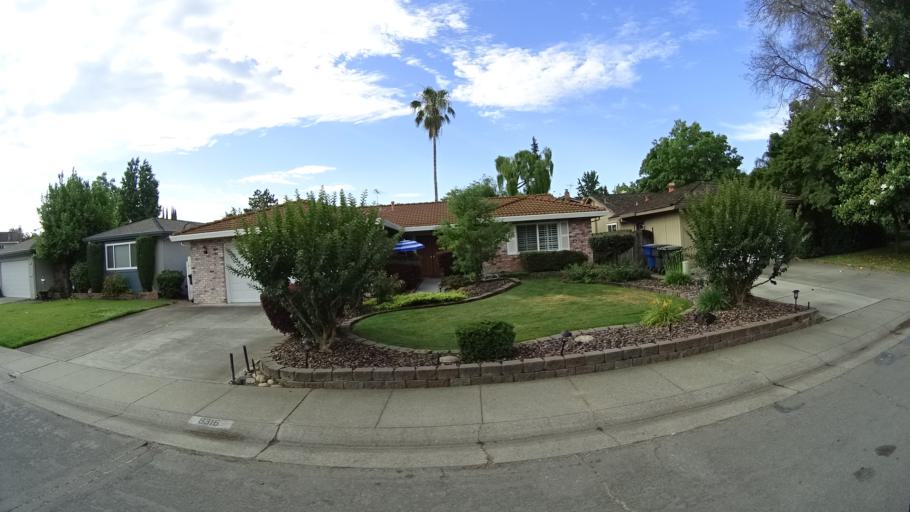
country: US
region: California
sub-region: Sacramento County
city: Rosemont
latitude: 38.5581
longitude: -121.3987
